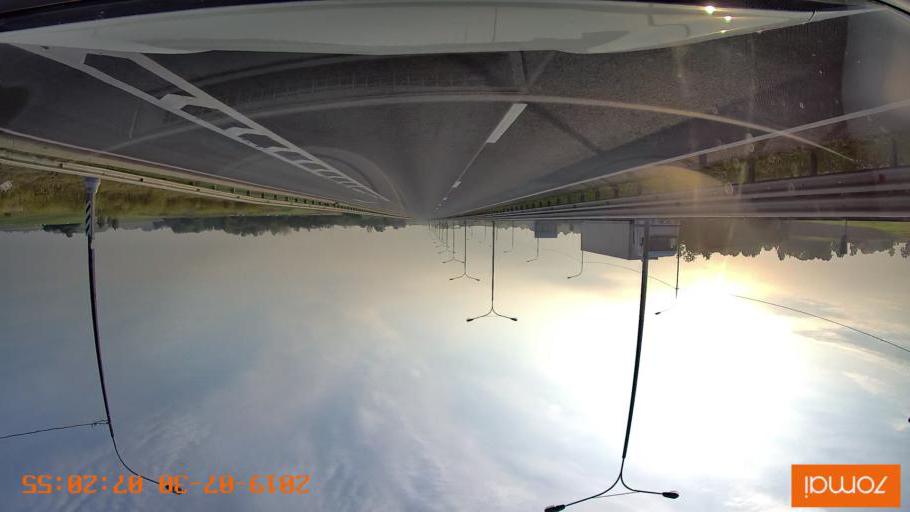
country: RU
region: Kaliningrad
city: Bol'shoe Isakovo
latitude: 54.6987
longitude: 20.7146
